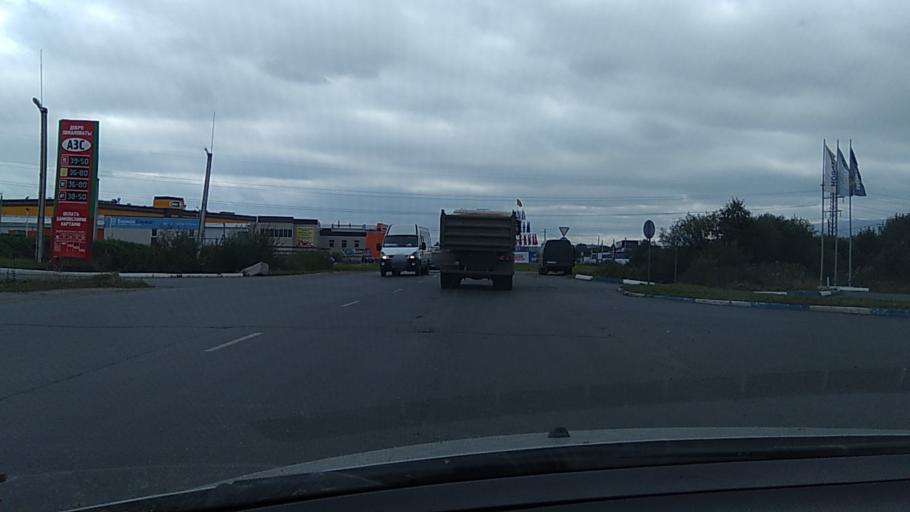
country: RU
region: Chelyabinsk
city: Zlatoust
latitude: 55.1180
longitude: 59.6985
